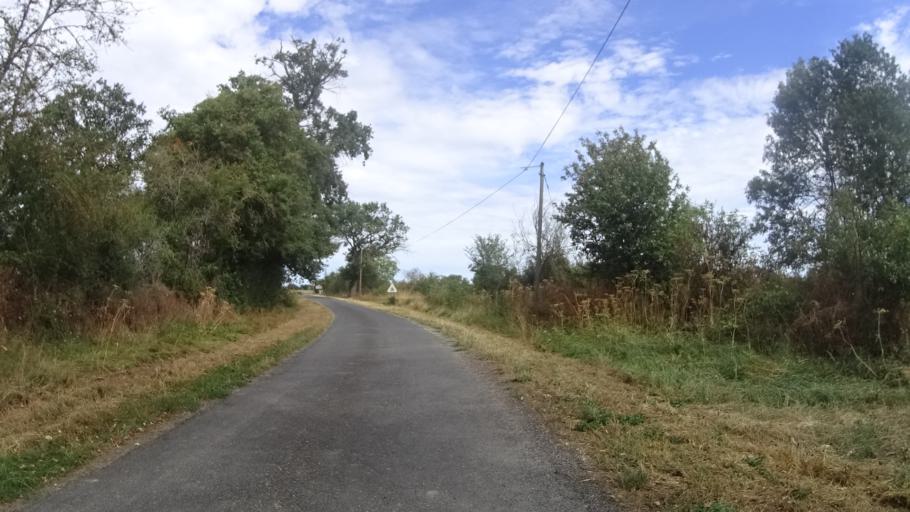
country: FR
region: Auvergne
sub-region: Departement de l'Allier
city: Beaulon
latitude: 46.6662
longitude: 3.6575
